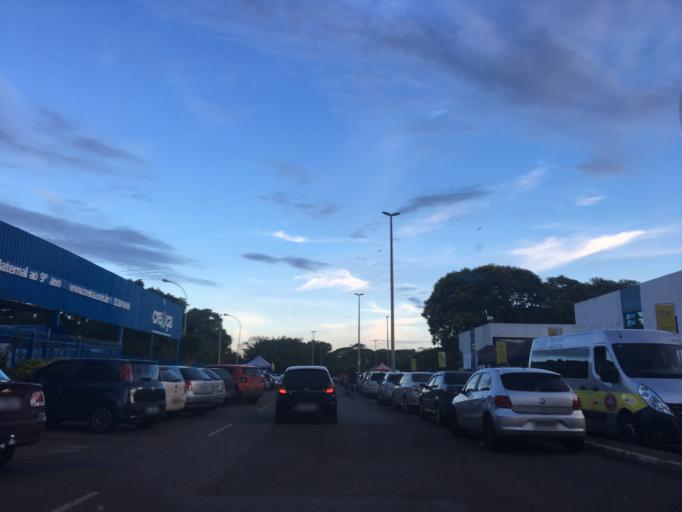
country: BR
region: Federal District
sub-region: Brasilia
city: Brasilia
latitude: -15.8016
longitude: -47.8996
